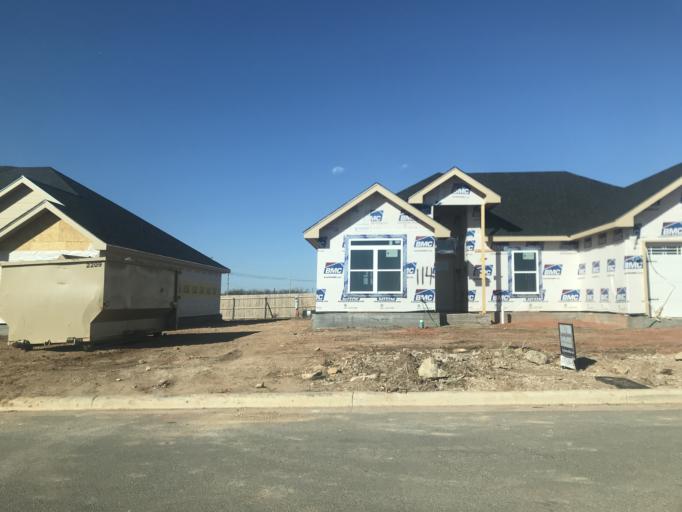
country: US
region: Texas
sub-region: Taylor County
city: Potosi
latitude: 32.3684
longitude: -99.7247
